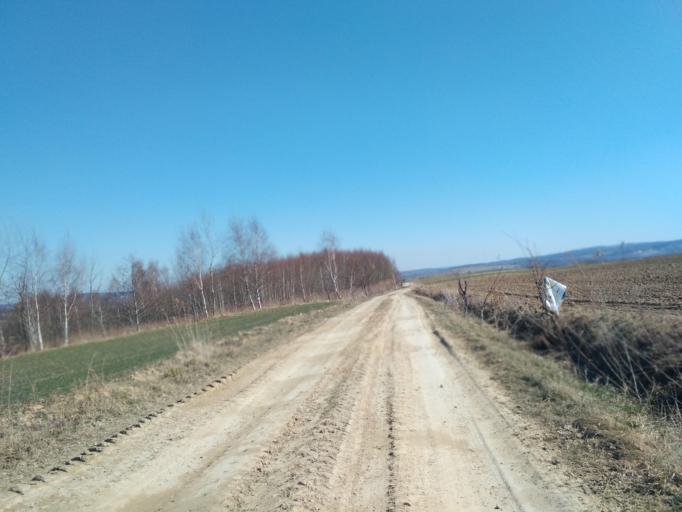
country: PL
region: Subcarpathian Voivodeship
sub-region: Powiat ropczycko-sedziszowski
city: Wielopole Skrzynskie
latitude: 49.9524
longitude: 21.5643
